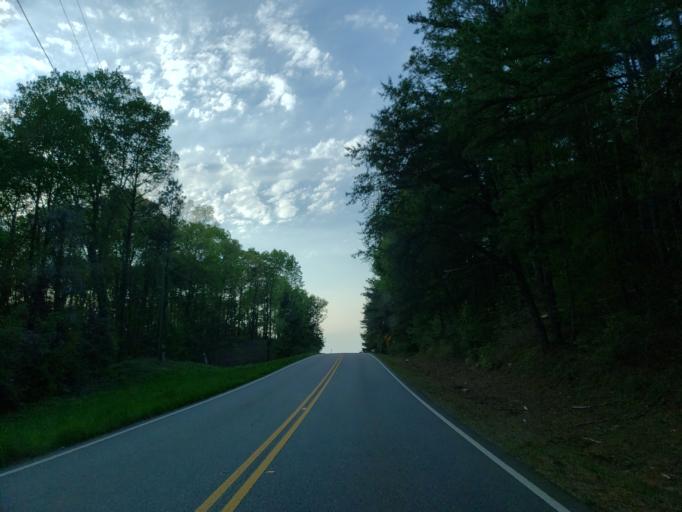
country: US
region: Georgia
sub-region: Cherokee County
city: Ball Ground
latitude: 34.2773
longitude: -84.3739
